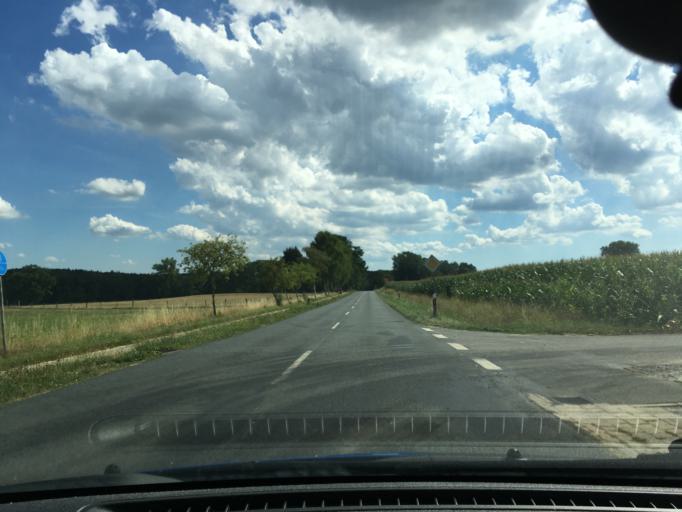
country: DE
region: Lower Saxony
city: Rehlingen
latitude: 53.1123
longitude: 10.2181
